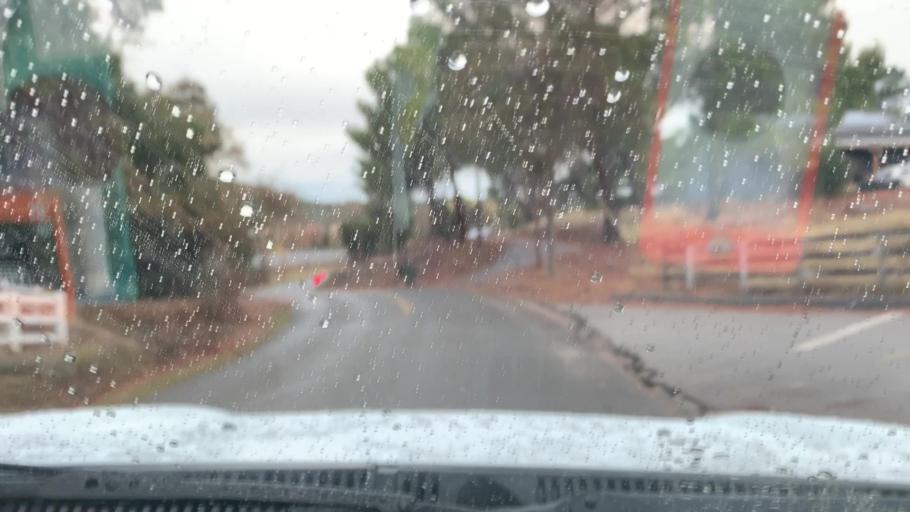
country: US
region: California
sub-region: San Luis Obispo County
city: Santa Margarita
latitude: 35.4379
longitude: -120.6361
